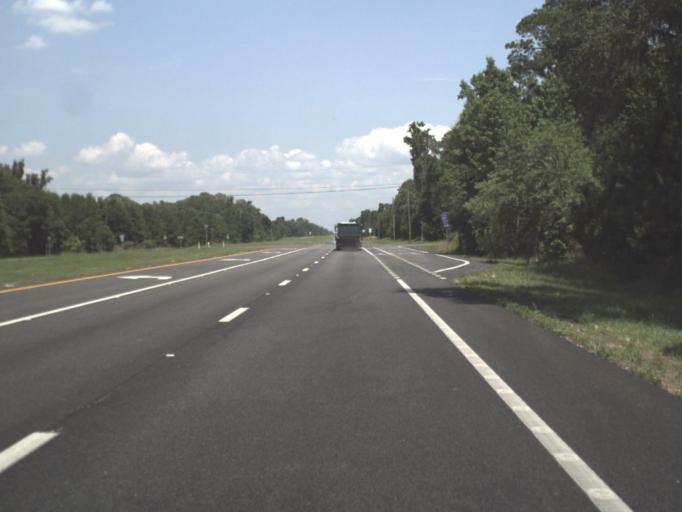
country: US
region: Florida
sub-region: Alachua County
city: Gainesville
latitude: 29.6102
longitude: -82.2435
